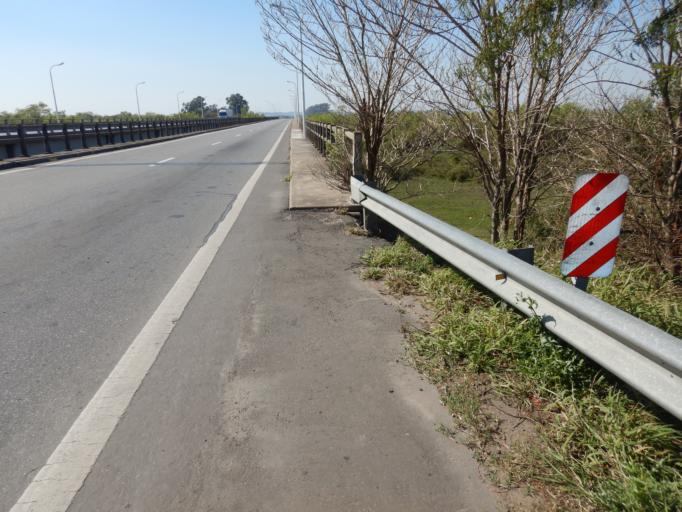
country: AR
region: Entre Rios
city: Parana
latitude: -31.6829
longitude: -60.5519
